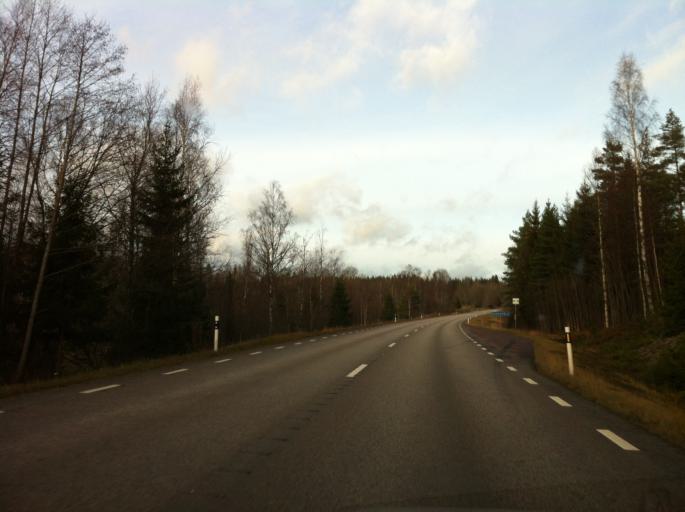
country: SE
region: Kronoberg
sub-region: Uppvidinge Kommun
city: Aseda
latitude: 57.1635
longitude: 15.3612
